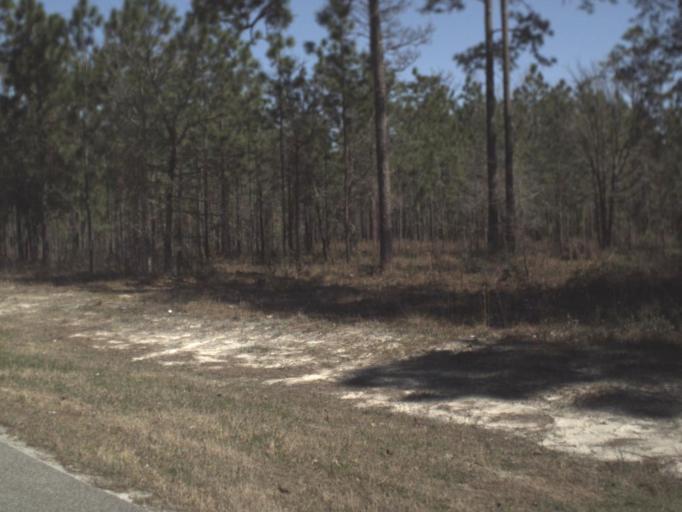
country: US
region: Florida
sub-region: Leon County
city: Woodville
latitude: 30.3382
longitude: -84.3112
